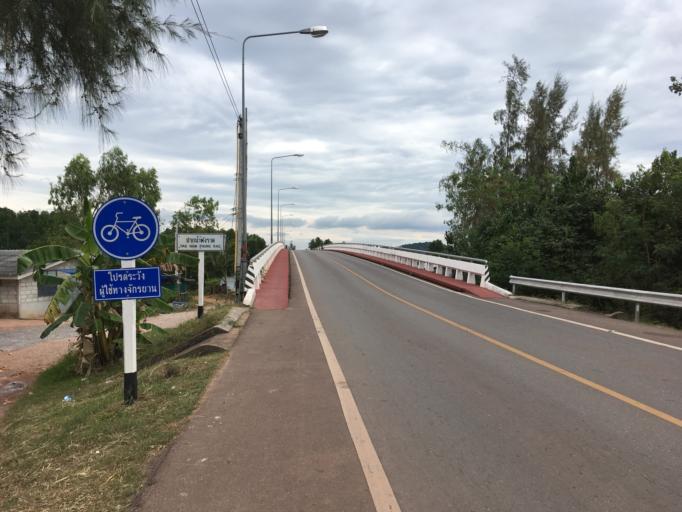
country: TH
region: Chanthaburi
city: Na Yai Am
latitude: 12.7067
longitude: 101.7850
